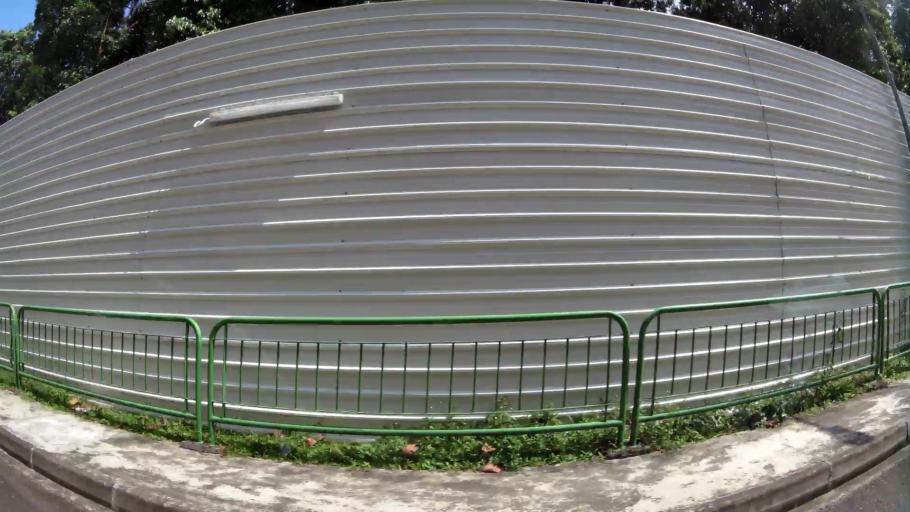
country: SG
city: Singapore
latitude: 1.3444
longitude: 103.8413
